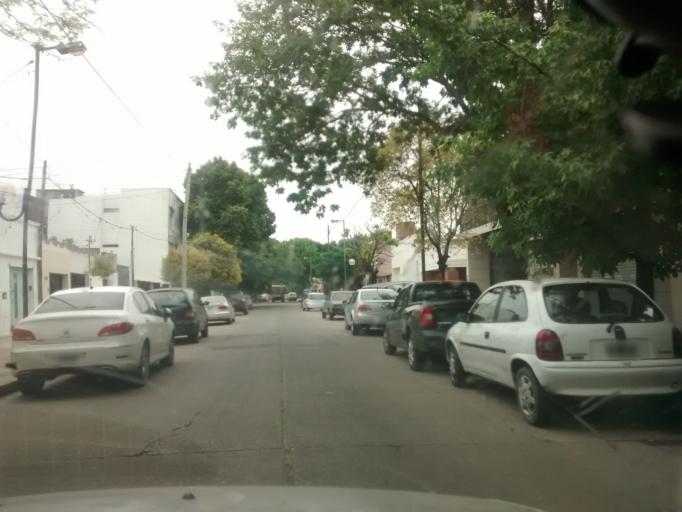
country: AR
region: Buenos Aires
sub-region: Partido de La Plata
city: La Plata
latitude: -34.9303
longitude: -57.9374
